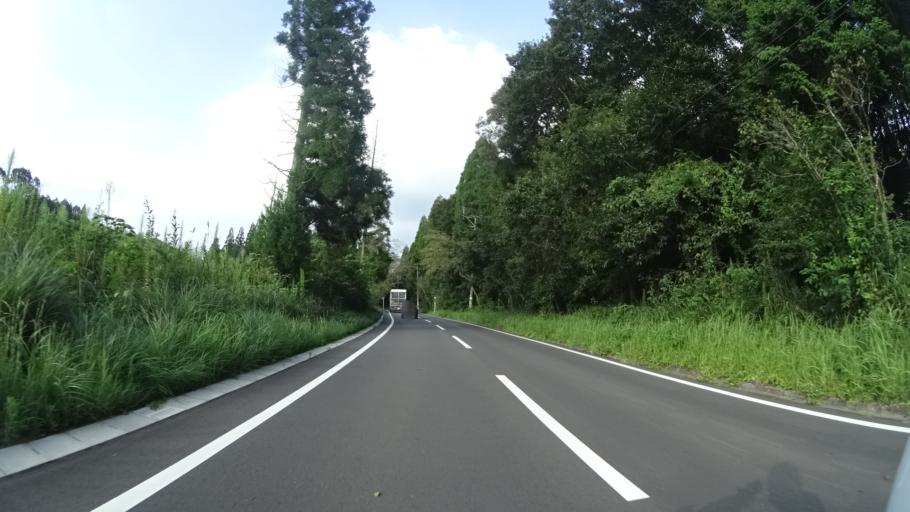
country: JP
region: Kagoshima
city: Okuchi-shinohara
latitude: 32.0206
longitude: 130.5896
